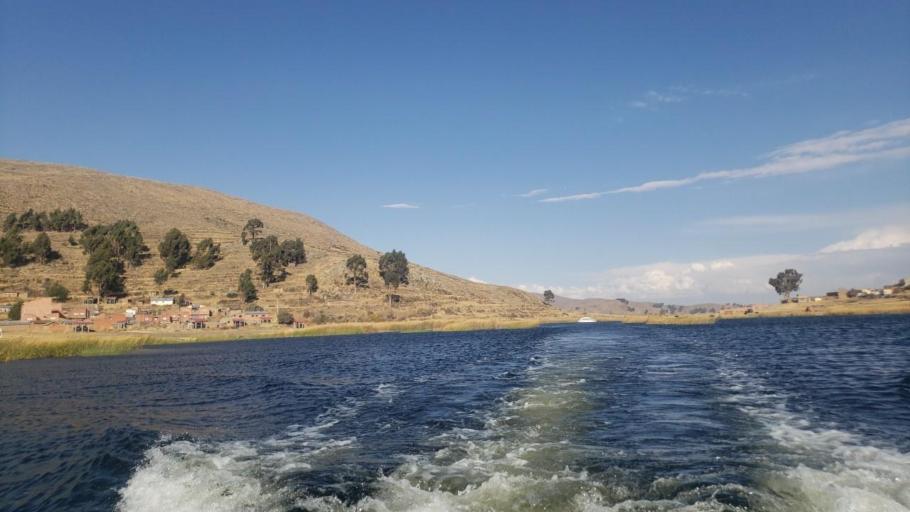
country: BO
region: La Paz
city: Huatajata
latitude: -16.3299
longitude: -68.7187
